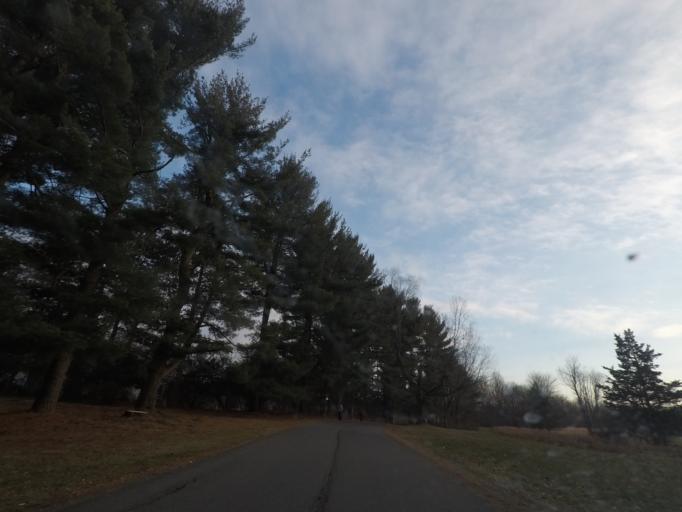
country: US
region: New York
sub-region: Rensselaer County
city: Wynantskill
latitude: 42.7269
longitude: -73.6494
